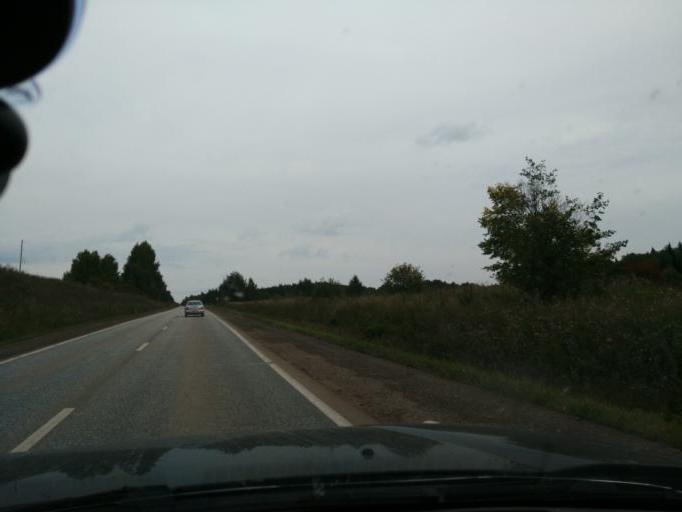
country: RU
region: Perm
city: Chernushka
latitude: 56.5755
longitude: 56.1330
